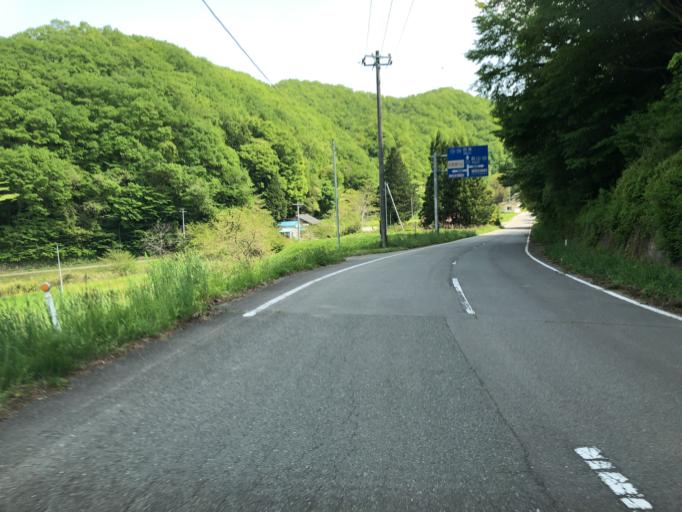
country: JP
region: Fukushima
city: Ishikawa
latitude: 36.9938
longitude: 140.6171
